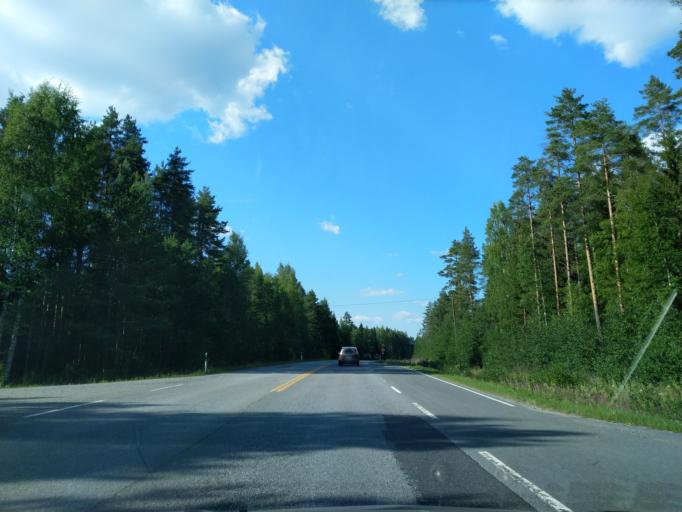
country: FI
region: Pirkanmaa
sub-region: Luoteis-Pirkanmaa
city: Kihnioe
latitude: 62.1660
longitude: 23.1616
